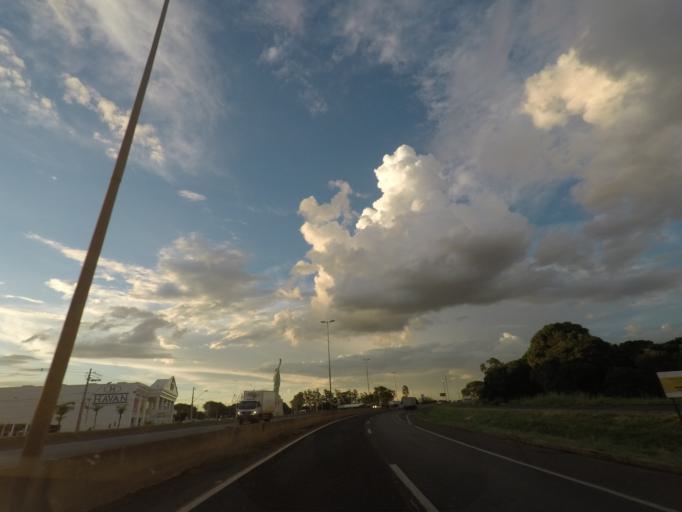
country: BR
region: Minas Gerais
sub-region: Uberaba
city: Uberaba
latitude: -19.7784
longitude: -47.9701
